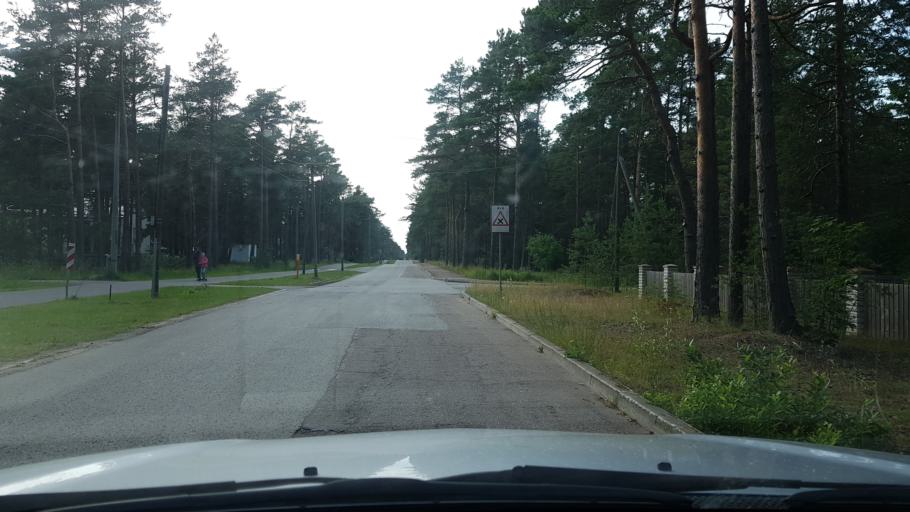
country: EE
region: Ida-Virumaa
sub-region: Narva-Joesuu linn
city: Narva-Joesuu
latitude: 59.4516
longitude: 28.0584
